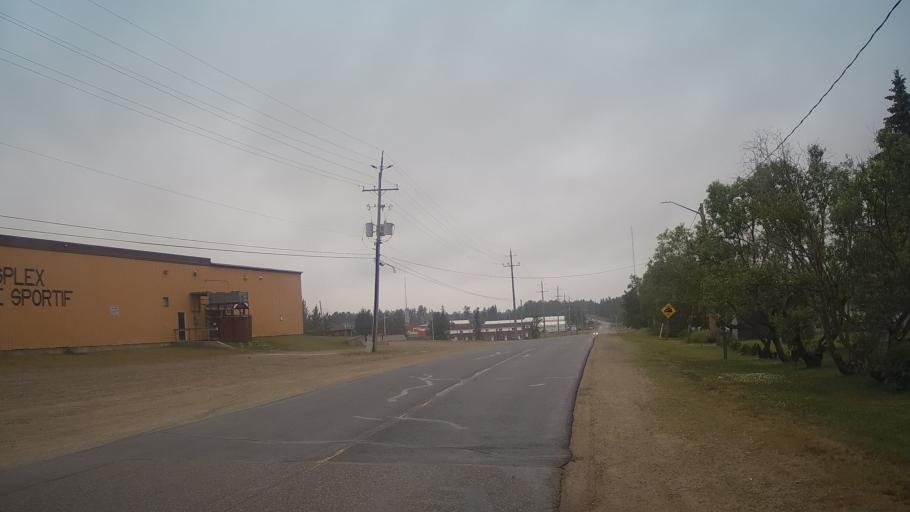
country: CA
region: Ontario
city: Greenstone
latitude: 49.7772
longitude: -86.5330
